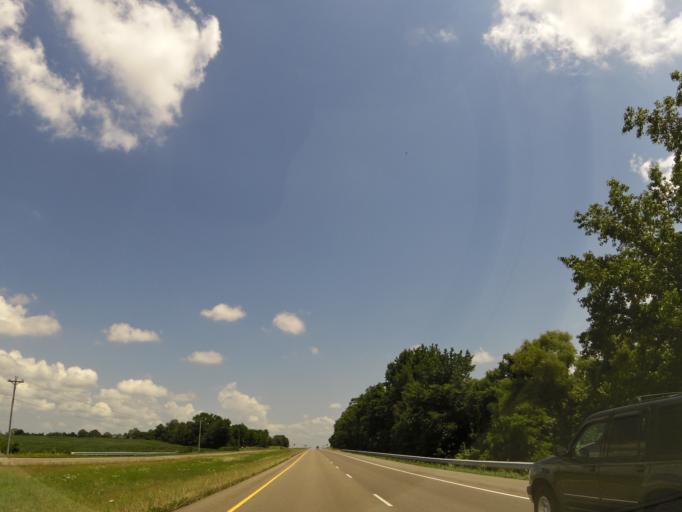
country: US
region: Tennessee
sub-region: Lauderdale County
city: Halls
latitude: 35.8966
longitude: -89.2436
